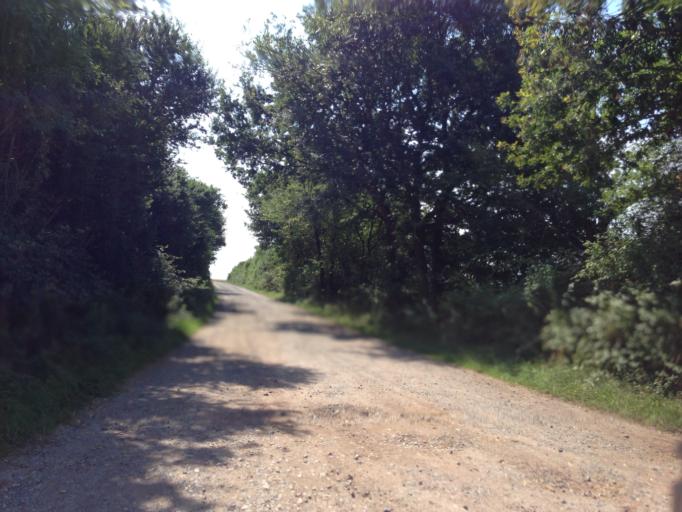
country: DE
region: Hesse
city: Dreieich
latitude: 50.0119
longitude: 8.7155
